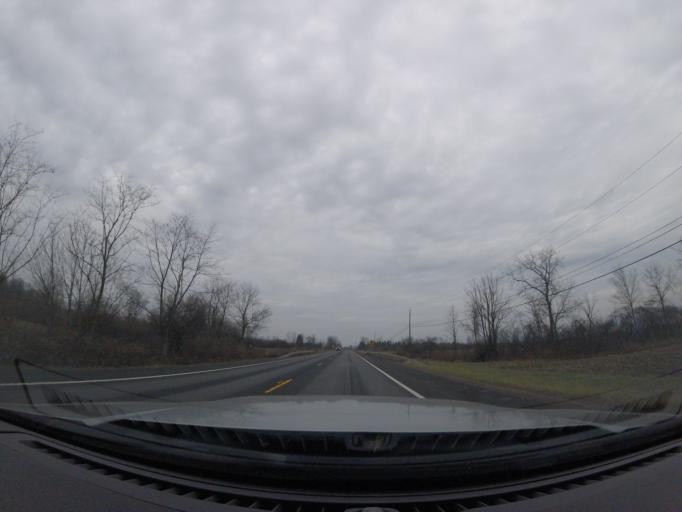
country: US
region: New York
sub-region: Schuyler County
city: Watkins Glen
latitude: 42.4406
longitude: -76.9078
